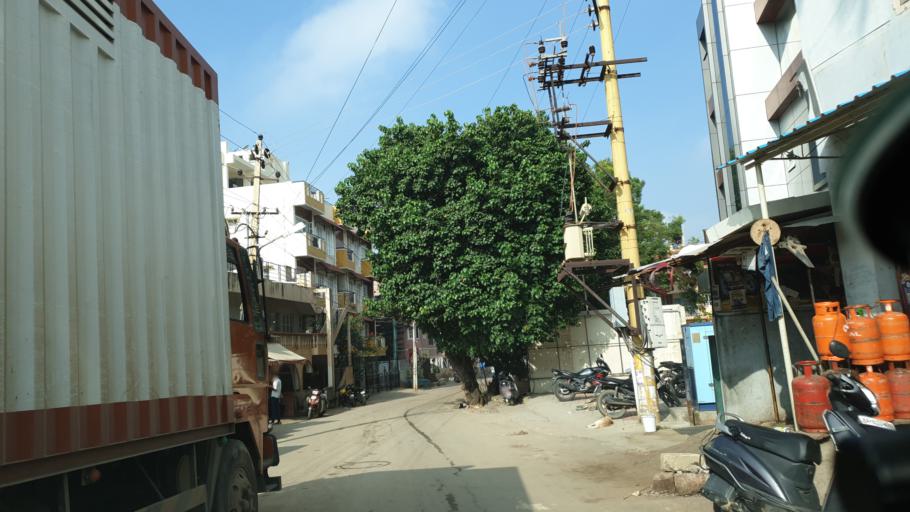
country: IN
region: Karnataka
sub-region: Bangalore Urban
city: Bangalore
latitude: 12.9715
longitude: 77.6926
